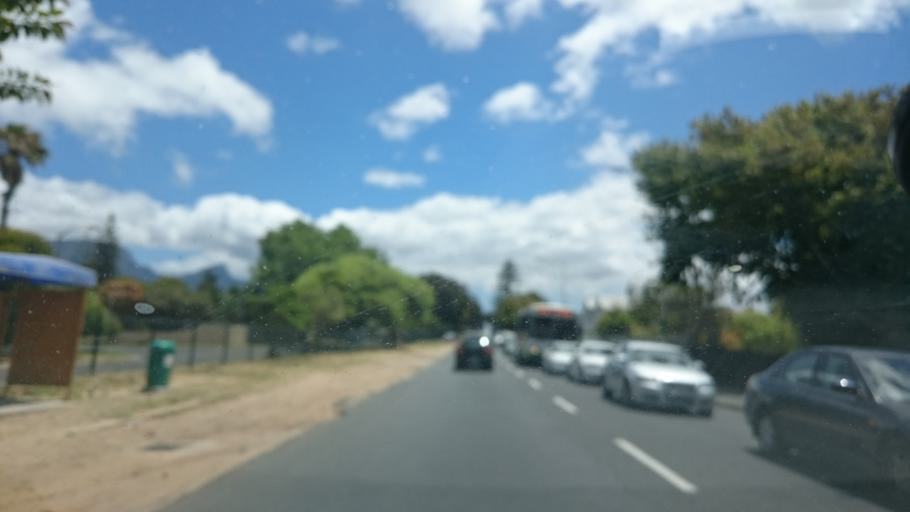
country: ZA
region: Western Cape
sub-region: City of Cape Town
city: Bergvliet
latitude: -34.0490
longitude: 18.4622
